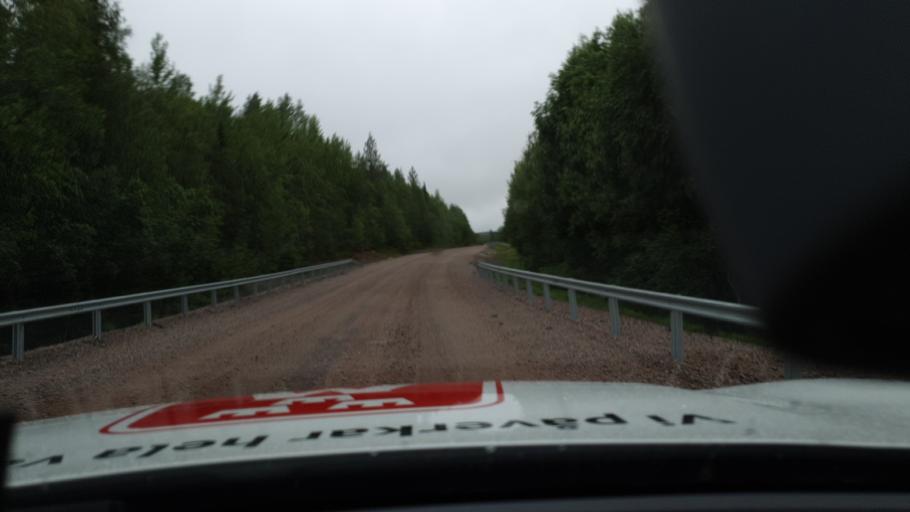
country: SE
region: Norrbotten
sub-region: Overtornea Kommun
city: OEvertornea
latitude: 66.5085
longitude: 23.4074
